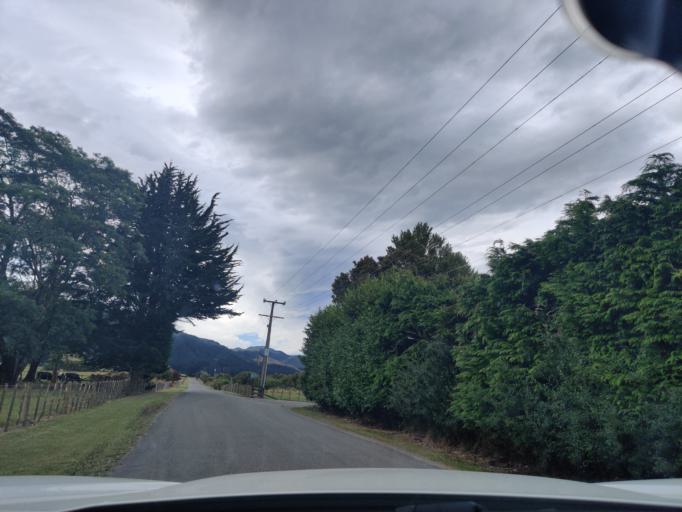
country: NZ
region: Wellington
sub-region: Masterton District
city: Masterton
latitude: -41.0363
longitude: 175.4460
